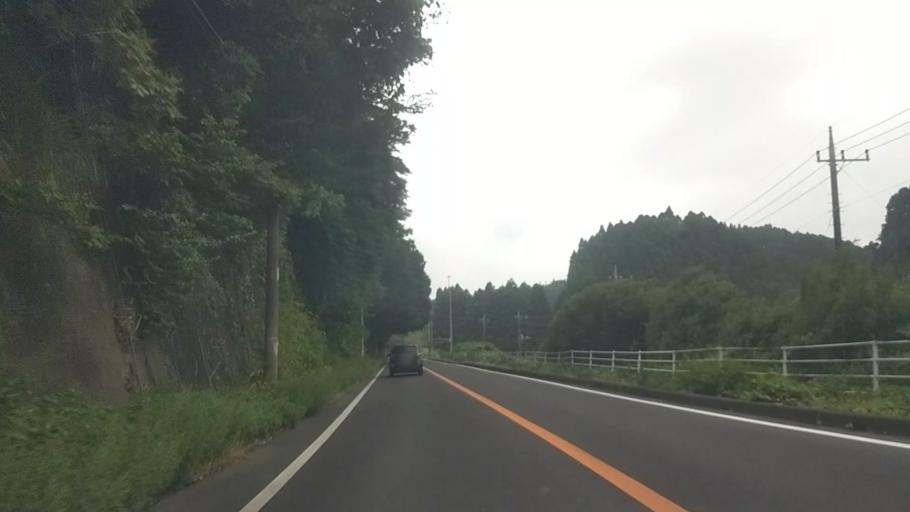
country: JP
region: Chiba
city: Ohara
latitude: 35.2652
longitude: 140.3615
